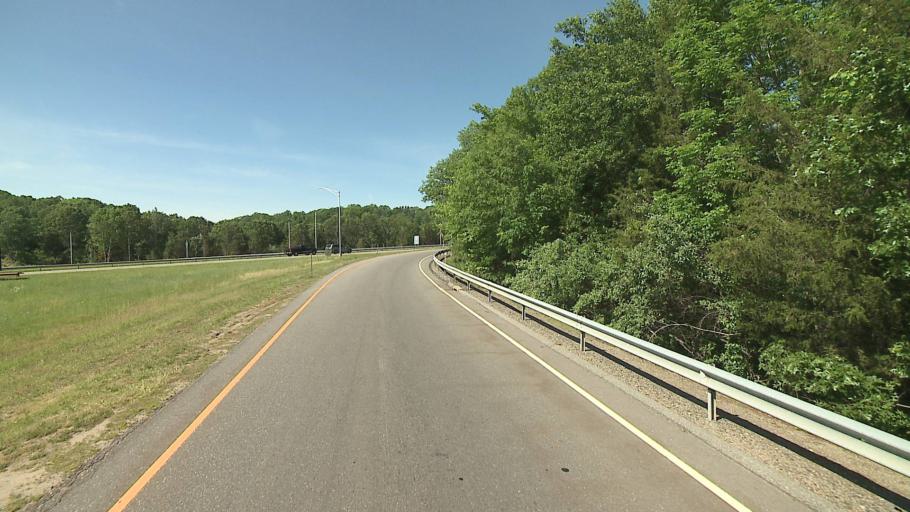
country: US
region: Connecticut
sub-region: New London County
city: Lisbon
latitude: 41.5857
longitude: -72.0507
